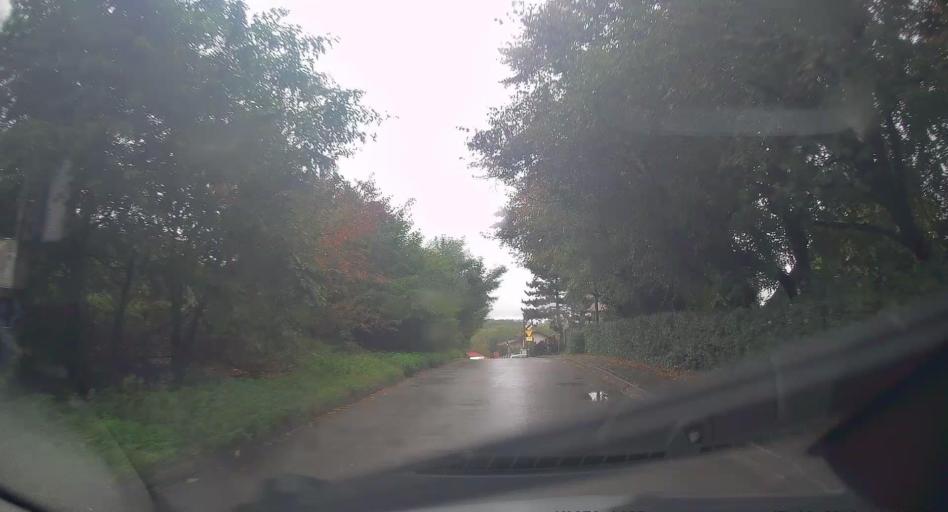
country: PL
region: Lesser Poland Voivodeship
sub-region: Powiat krakowski
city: Ochojno
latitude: 50.0026
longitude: 19.9934
